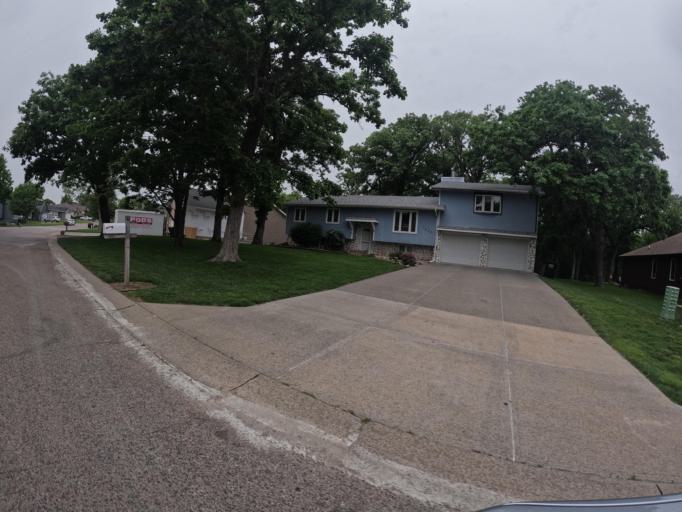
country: US
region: Nebraska
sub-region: Sarpy County
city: Offutt Air Force Base
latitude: 41.0488
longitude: -95.9708
